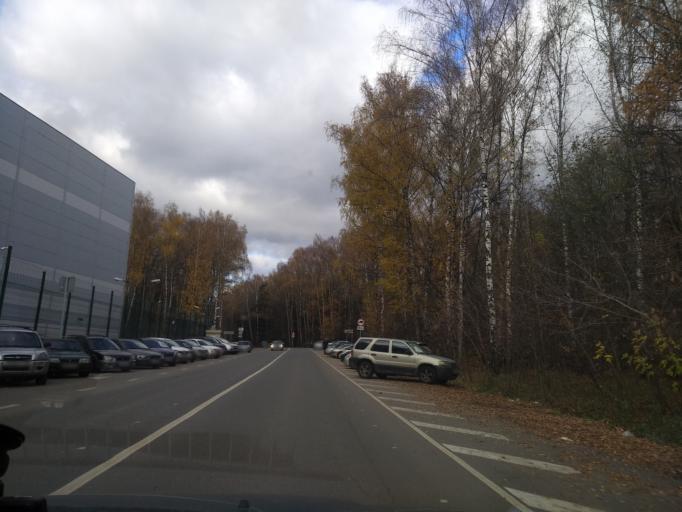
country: RU
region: Moscow
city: Bibirevo
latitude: 55.9065
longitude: 37.6122
